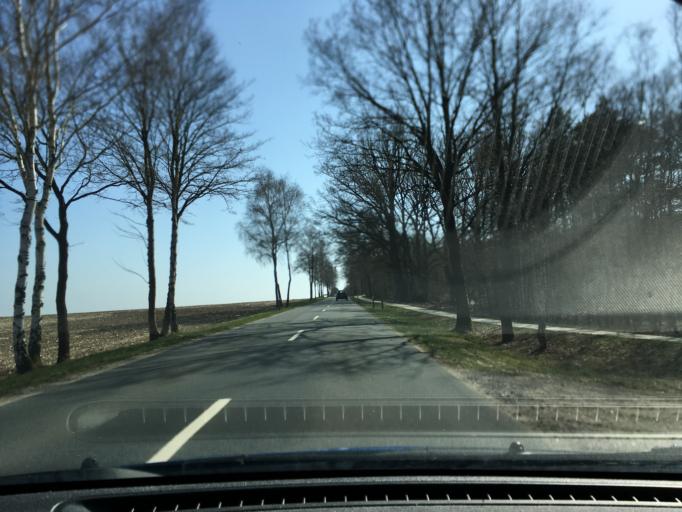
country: DE
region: Lower Saxony
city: Eimke
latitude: 52.9872
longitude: 10.3072
